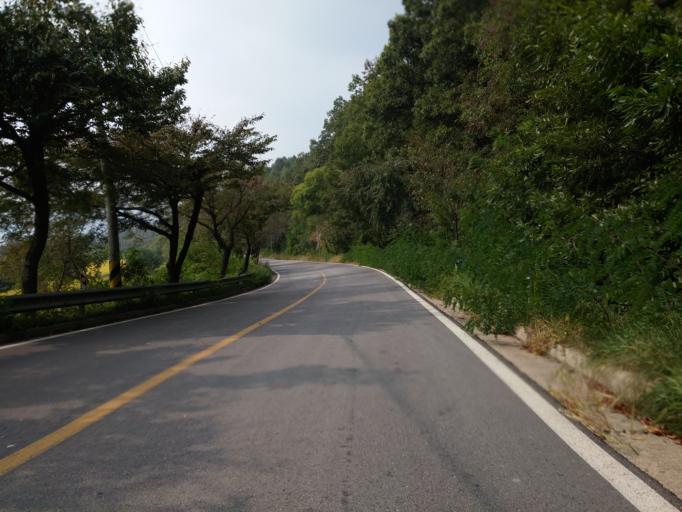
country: KR
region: Chungcheongbuk-do
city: Yong-dong
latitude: 36.3426
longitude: 127.8117
